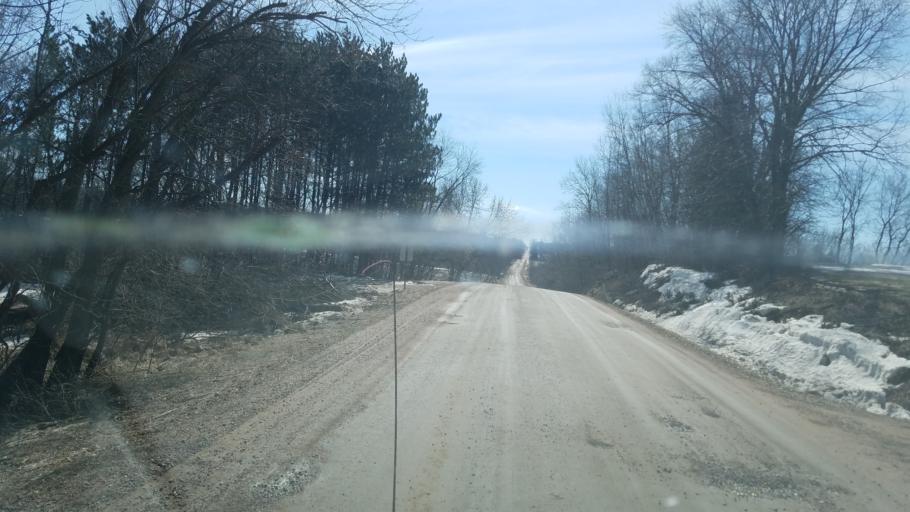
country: US
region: Wisconsin
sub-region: Clark County
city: Neillsville
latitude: 44.5939
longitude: -90.4566
